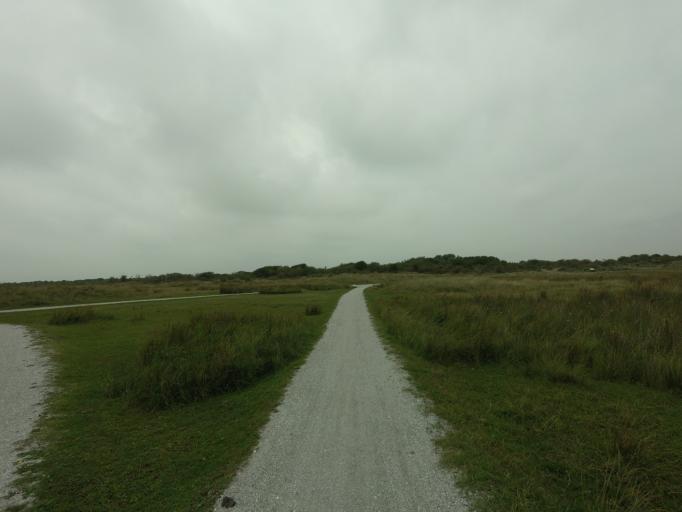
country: NL
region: Friesland
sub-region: Gemeente Schiermonnikoog
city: Schiermonnikoog
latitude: 53.4861
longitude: 6.2182
